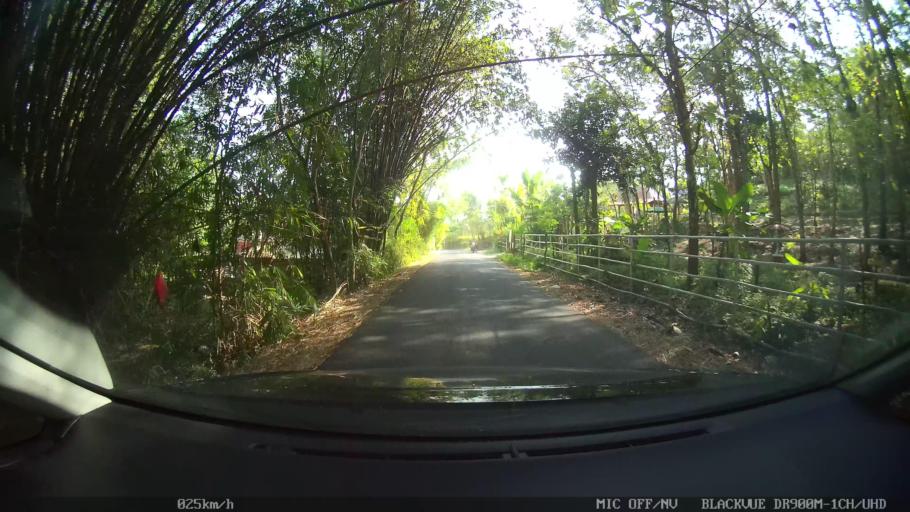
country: ID
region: Daerah Istimewa Yogyakarta
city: Kasihan
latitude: -7.8385
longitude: 110.3357
